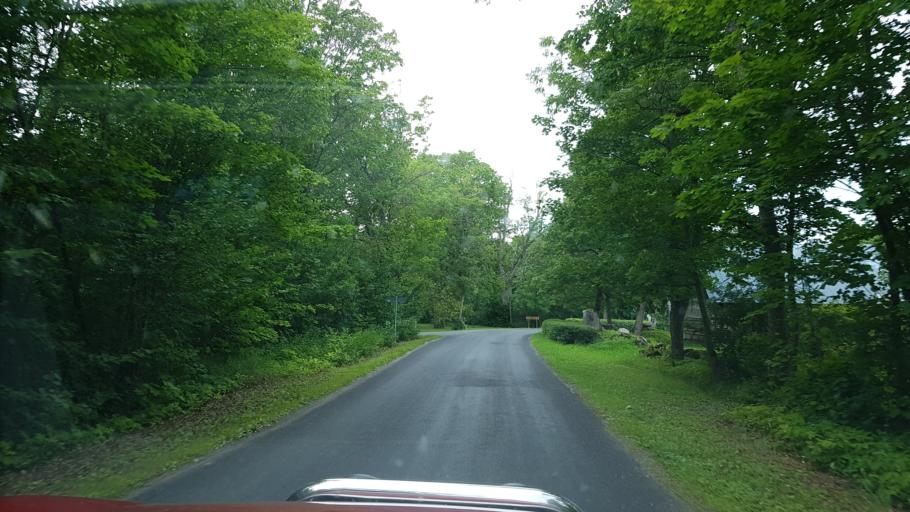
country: EE
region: Laeaene
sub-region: Ridala Parish
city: Uuemoisa
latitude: 59.0007
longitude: 23.7223
